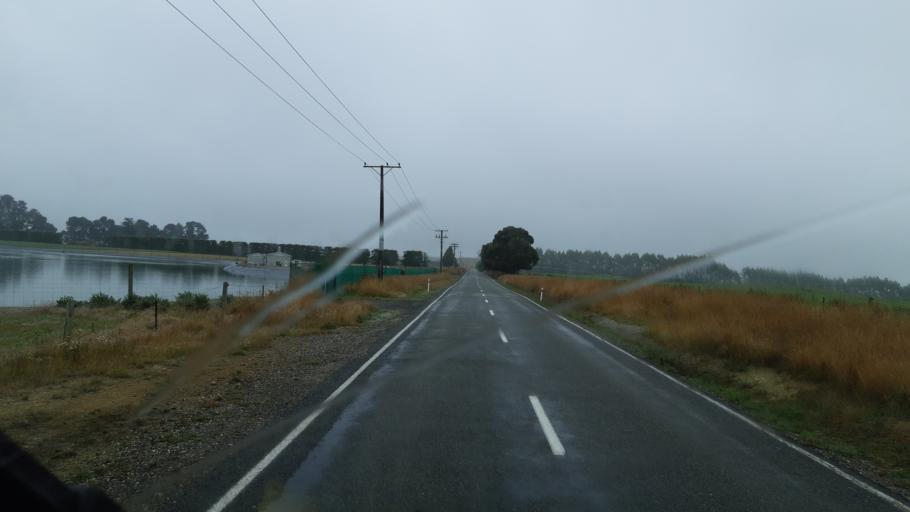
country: NZ
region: Otago
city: Oamaru
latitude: -44.9300
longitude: 170.7888
